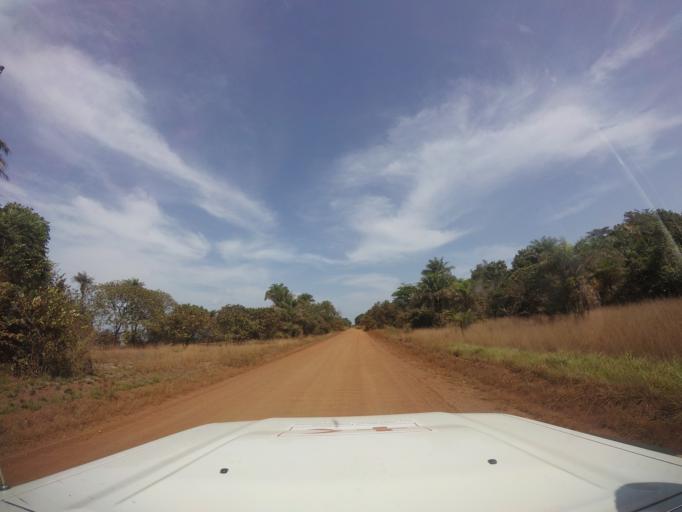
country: LR
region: Grand Cape Mount
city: Robertsport
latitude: 6.6864
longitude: -11.2480
